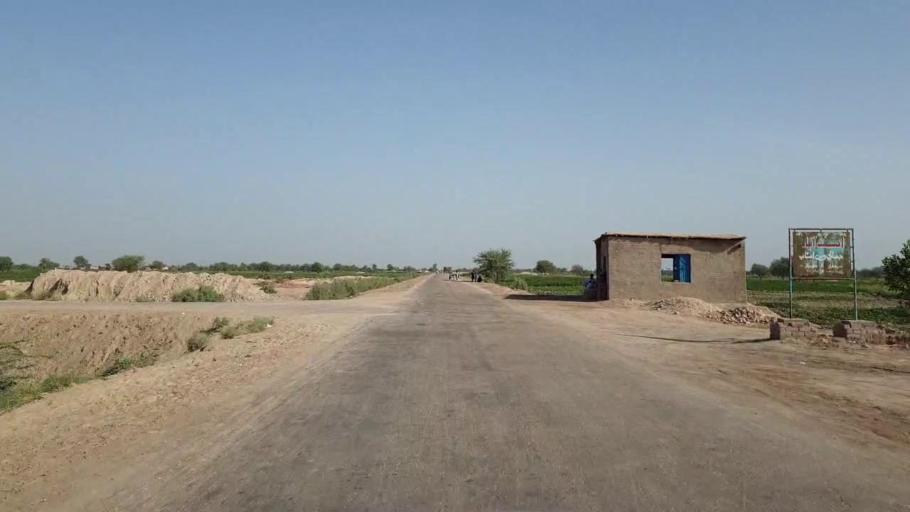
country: PK
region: Sindh
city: Nawabshah
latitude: 26.1407
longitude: 68.4520
